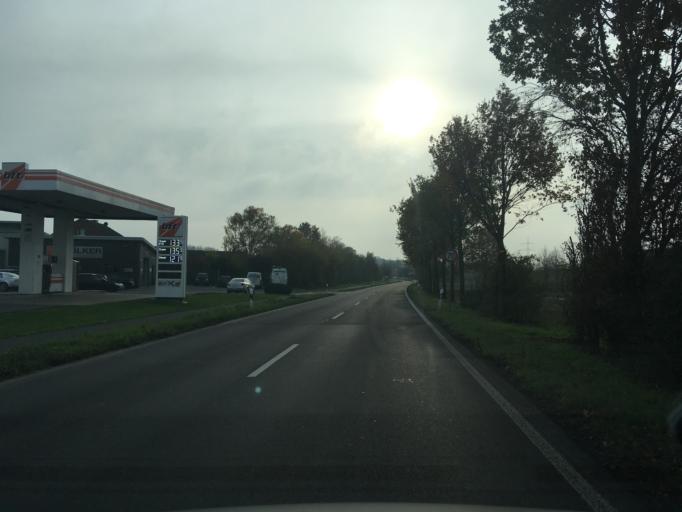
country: DE
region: North Rhine-Westphalia
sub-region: Regierungsbezirk Munster
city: Velen
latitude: 51.8973
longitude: 6.9743
